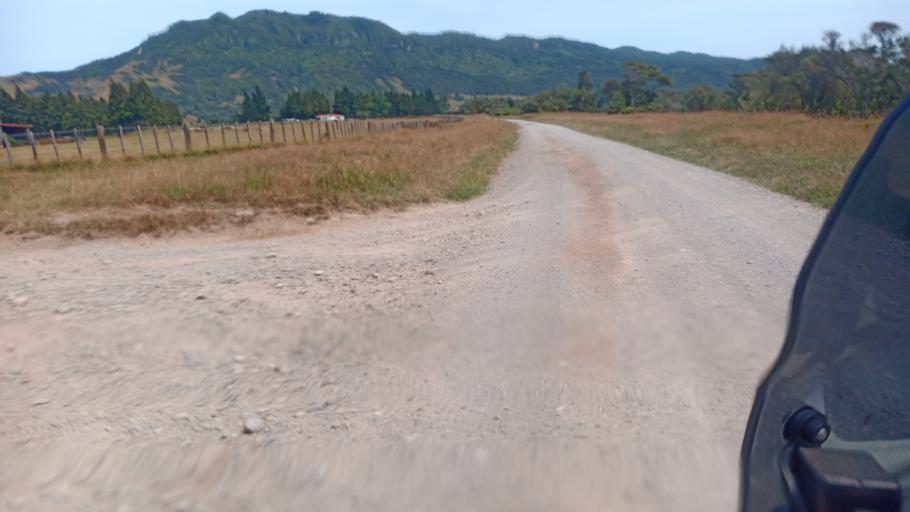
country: NZ
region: Bay of Plenty
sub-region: Opotiki District
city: Opotiki
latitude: -37.6546
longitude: 178.1121
